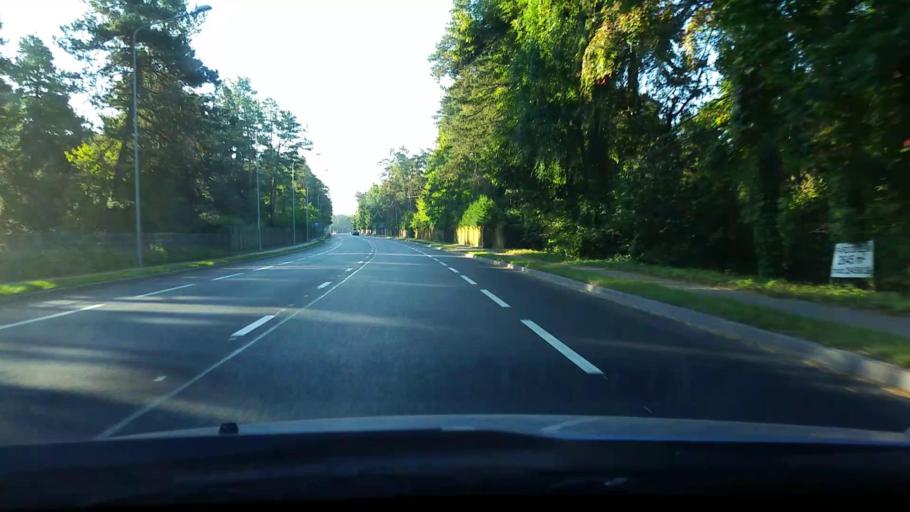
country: LV
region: Adazi
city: Adazi
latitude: 57.0383
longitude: 24.3159
